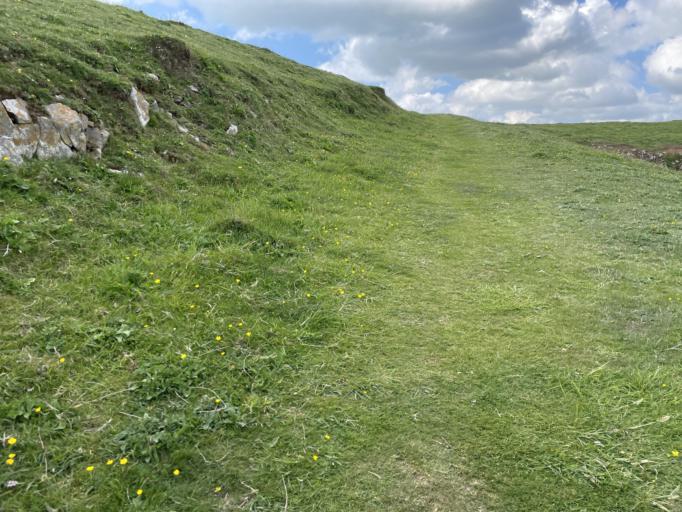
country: GB
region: Wales
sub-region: Pembrokeshire
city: Castlemartin
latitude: 51.6118
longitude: -4.9906
